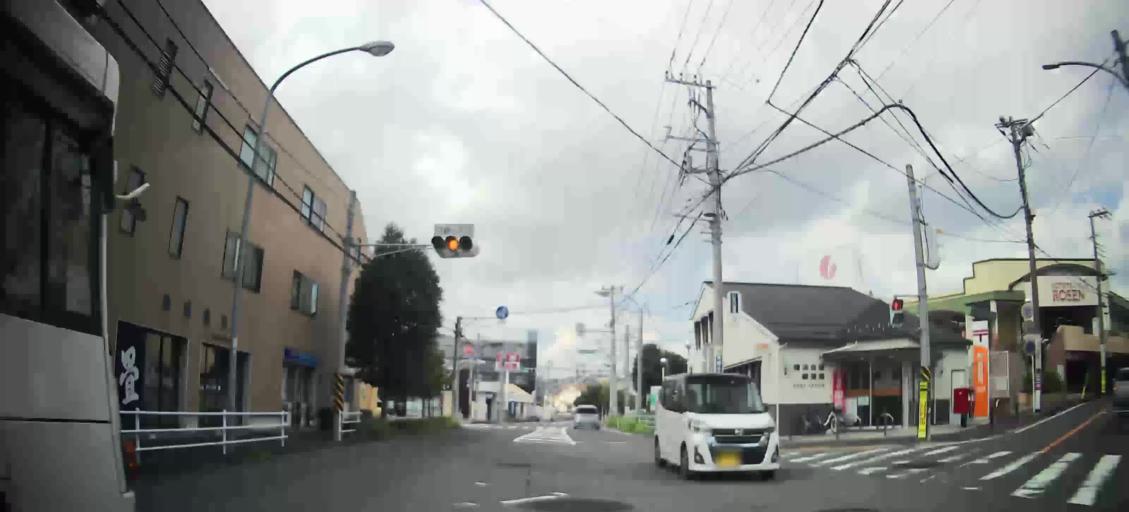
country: JP
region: Kanagawa
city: Minami-rinkan
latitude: 35.4875
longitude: 139.5432
